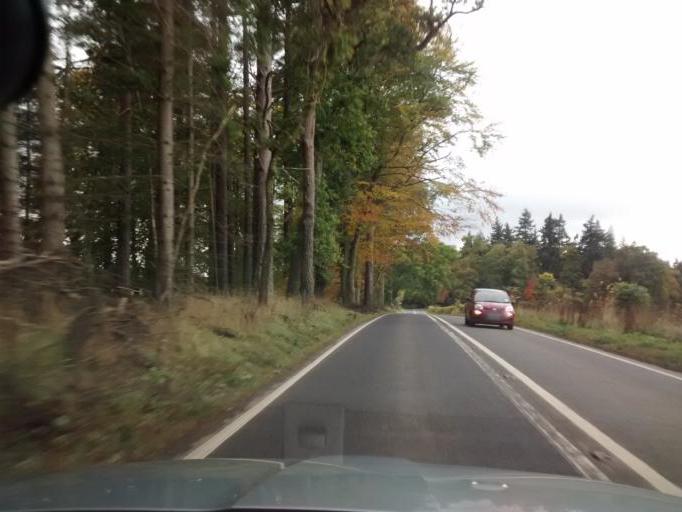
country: GB
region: Scotland
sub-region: Perth and Kinross
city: Blairgowrie
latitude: 56.5377
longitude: -3.3616
